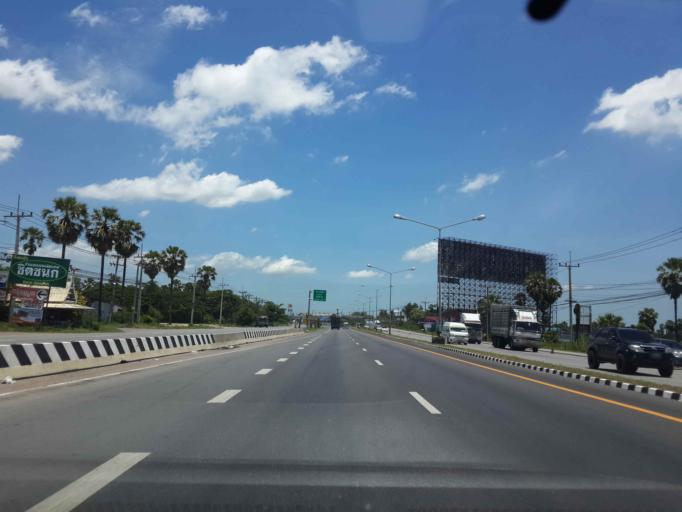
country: TH
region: Phetchaburi
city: Ban Lat
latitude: 13.0530
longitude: 99.9417
